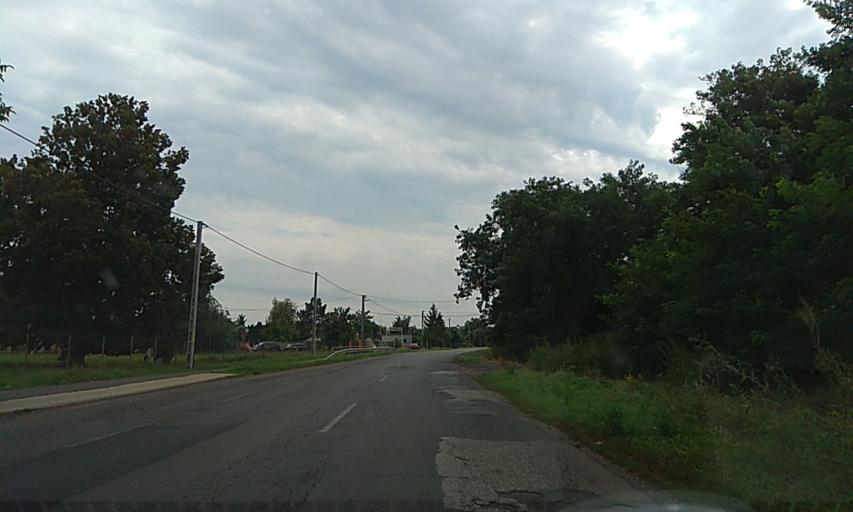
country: HU
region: Szabolcs-Szatmar-Bereg
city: Nyiregyhaza
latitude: 47.9983
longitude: 21.7018
